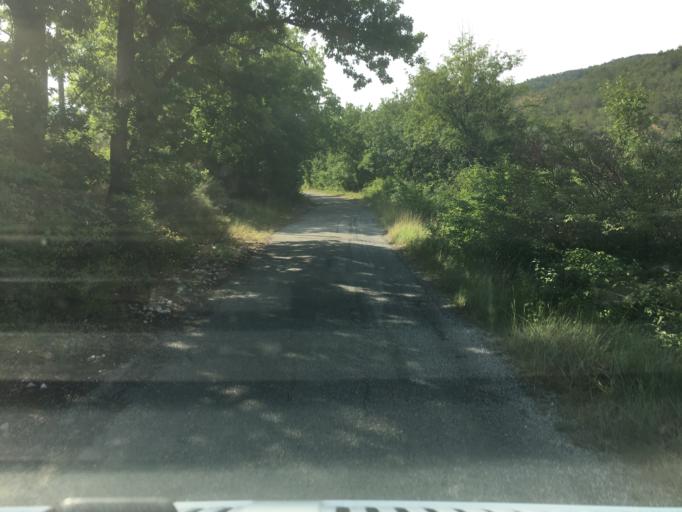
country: FR
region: Provence-Alpes-Cote d'Azur
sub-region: Departement des Alpes-de-Haute-Provence
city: Riez
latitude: 43.9158
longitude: 6.1927
